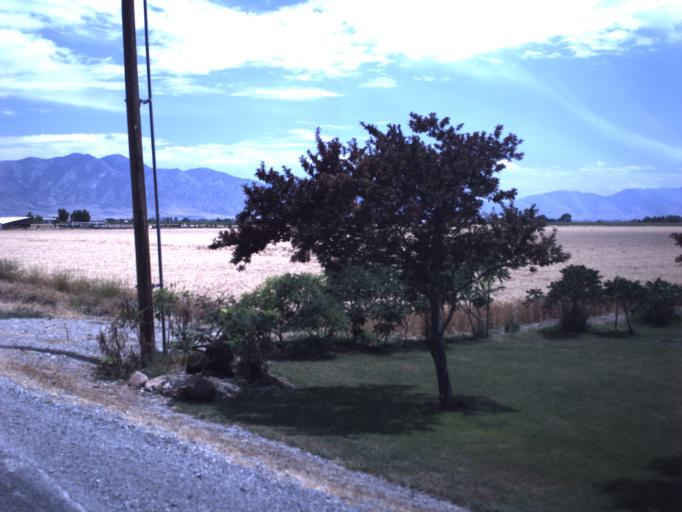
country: US
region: Utah
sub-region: Box Elder County
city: Tremonton
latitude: 41.7098
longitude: -112.2516
